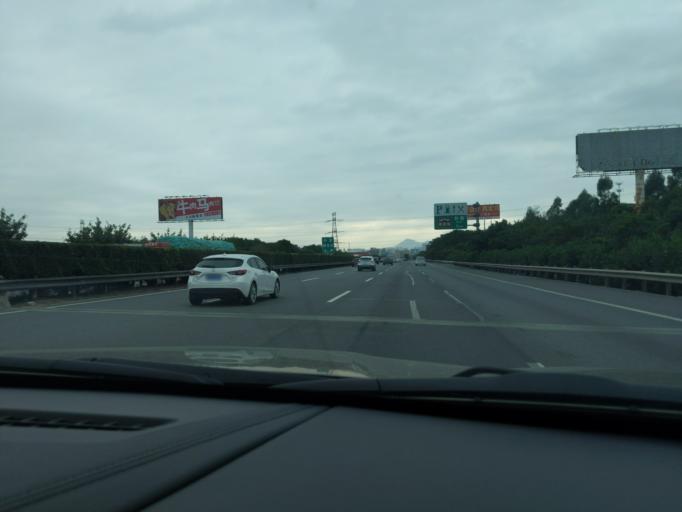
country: CN
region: Fujian
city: Neikeng
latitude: 24.7654
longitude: 118.4501
